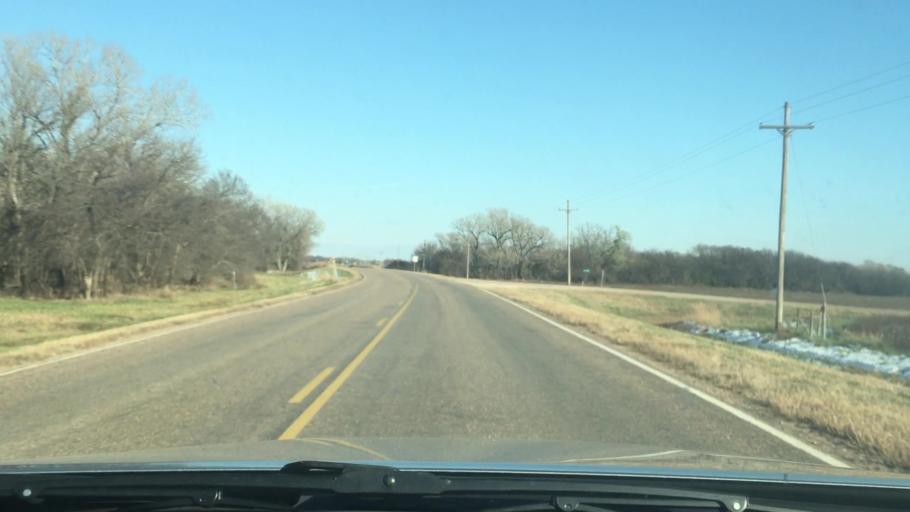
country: US
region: Kansas
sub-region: Rice County
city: Lyons
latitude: 38.2892
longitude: -98.1474
